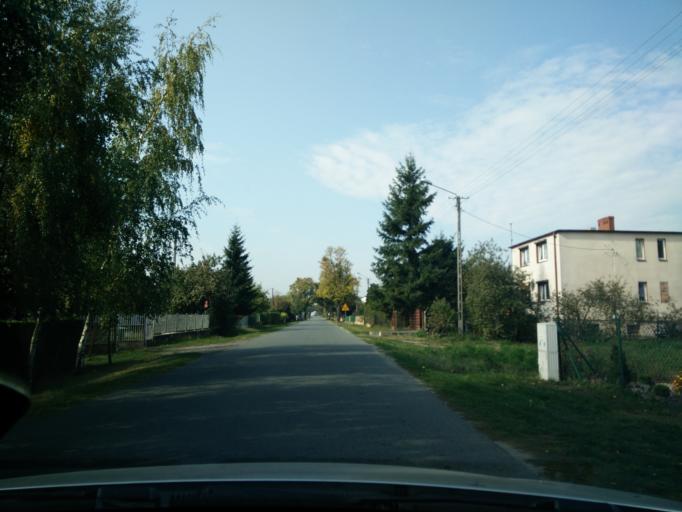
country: PL
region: Greater Poland Voivodeship
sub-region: Powiat sredzki
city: Dominowo
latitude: 52.3040
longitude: 17.2854
